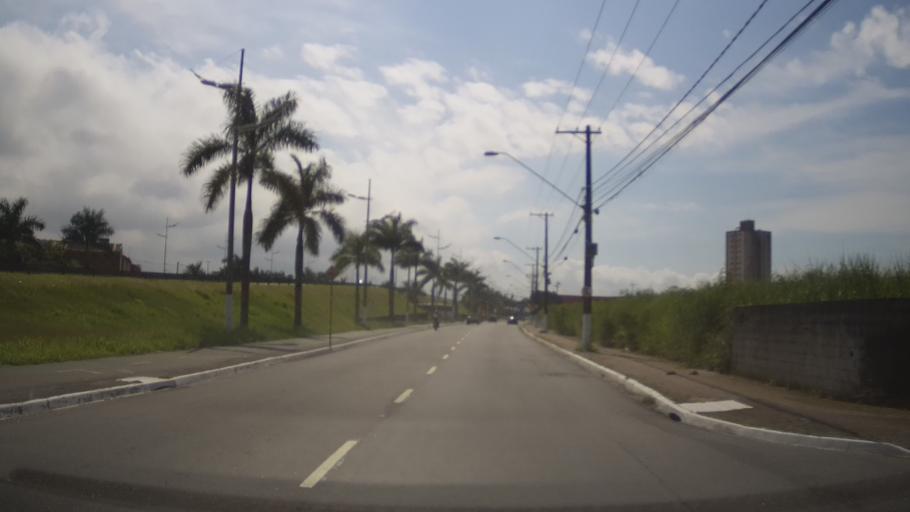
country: BR
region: Sao Paulo
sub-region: Praia Grande
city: Praia Grande
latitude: -24.0286
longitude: -46.5003
